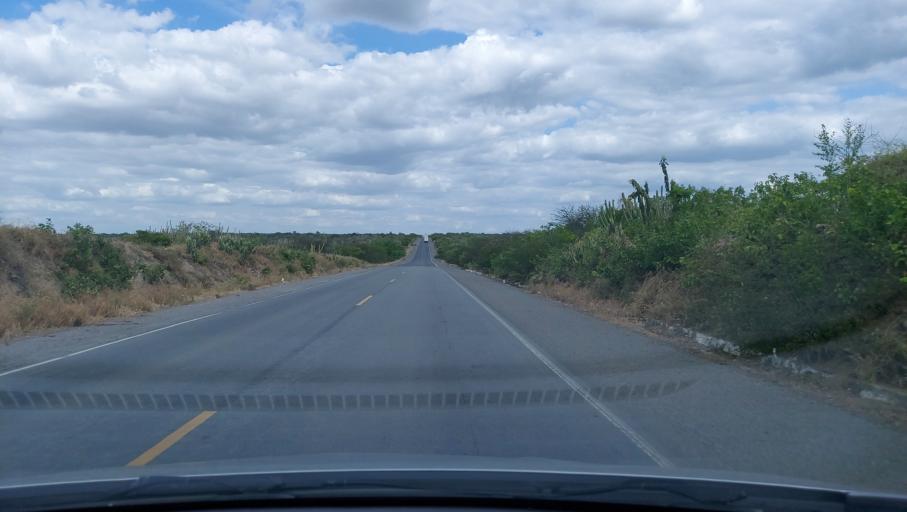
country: BR
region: Bahia
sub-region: Ipira
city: Ipira
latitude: -12.4911
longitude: -39.8078
